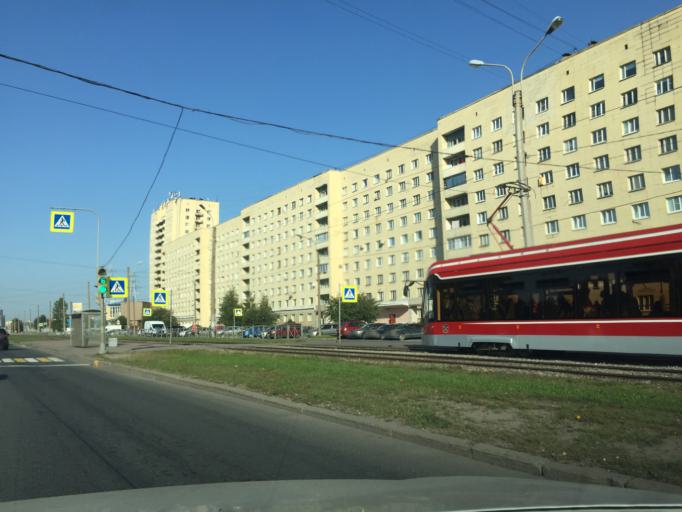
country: RU
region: St.-Petersburg
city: Grazhdanka
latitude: 60.0120
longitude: 30.4342
